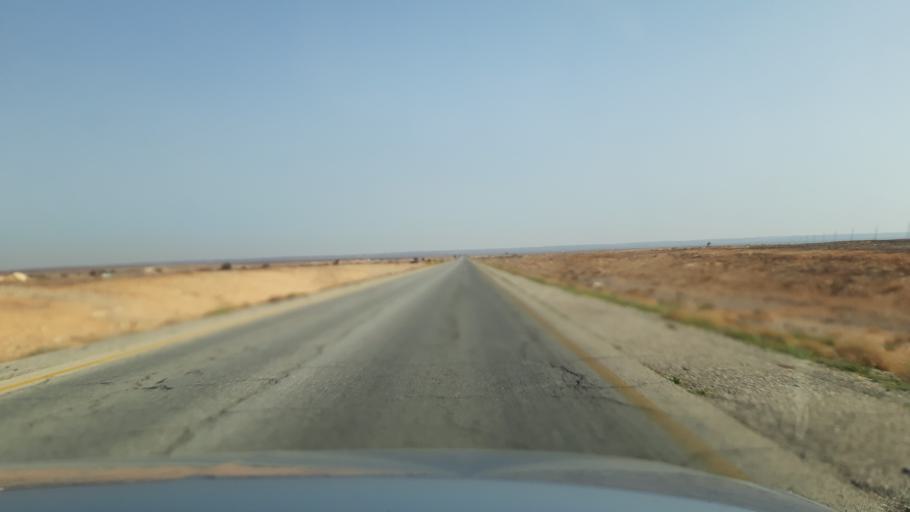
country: JO
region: Amman
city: Al Azraq ash Shamali
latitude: 31.7909
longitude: 36.5827
